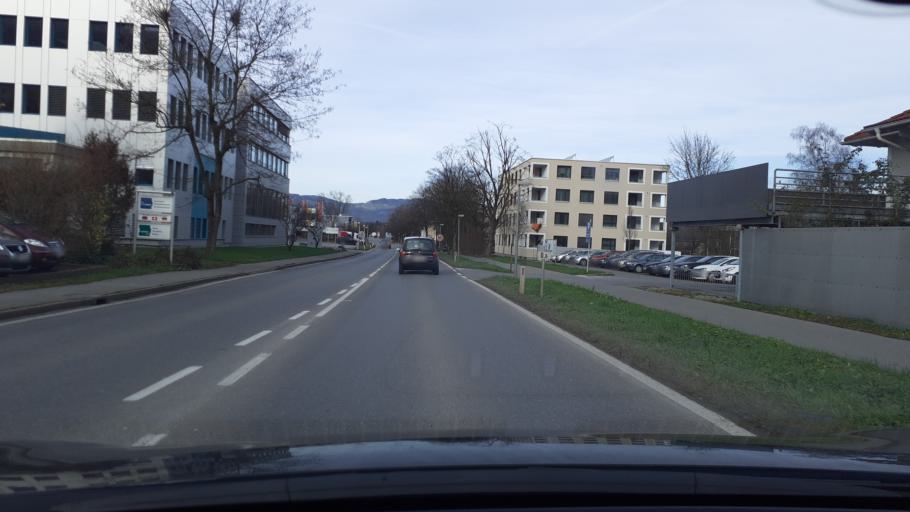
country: AT
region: Vorarlberg
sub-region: Politischer Bezirk Dornbirn
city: Hohenems
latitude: 47.3706
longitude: 9.6839
